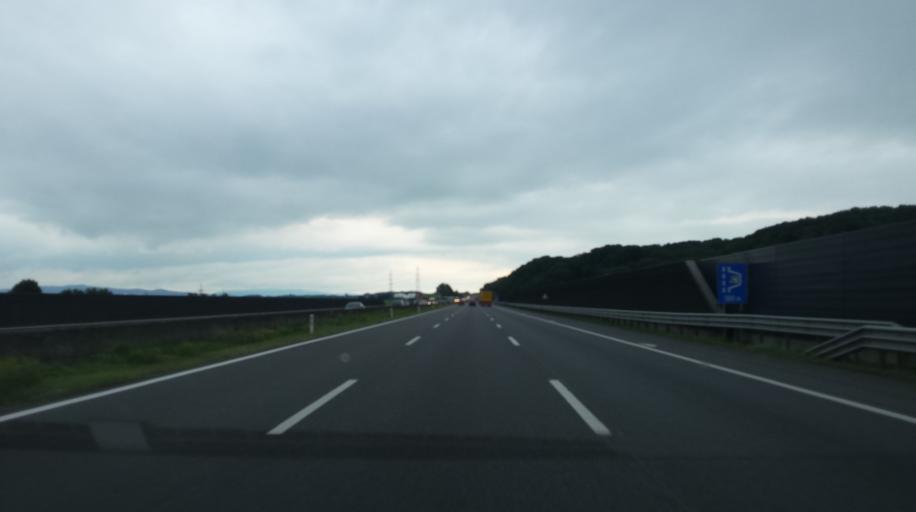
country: AT
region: Lower Austria
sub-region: Politischer Bezirk Melk
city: Ybbs an der Donau
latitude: 48.1436
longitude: 15.0738
